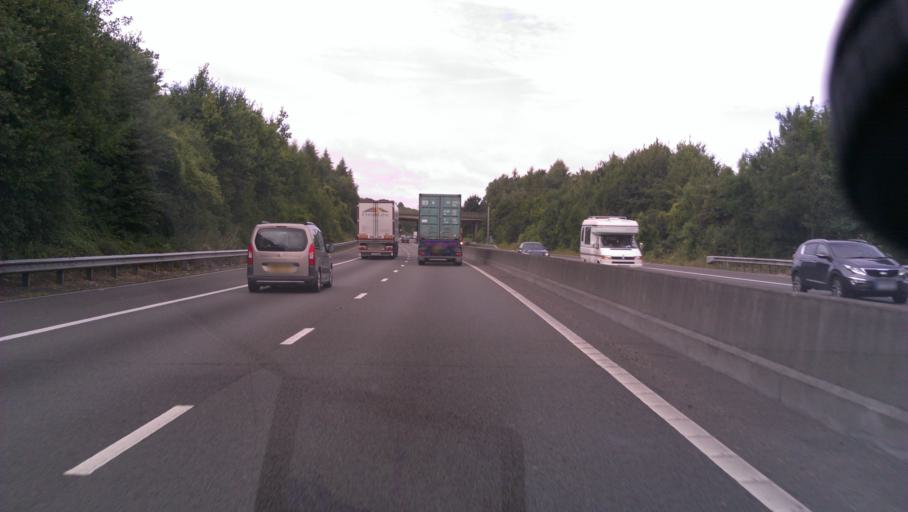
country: GB
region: England
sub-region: Essex
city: Elsenham
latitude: 51.9086
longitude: 0.2221
